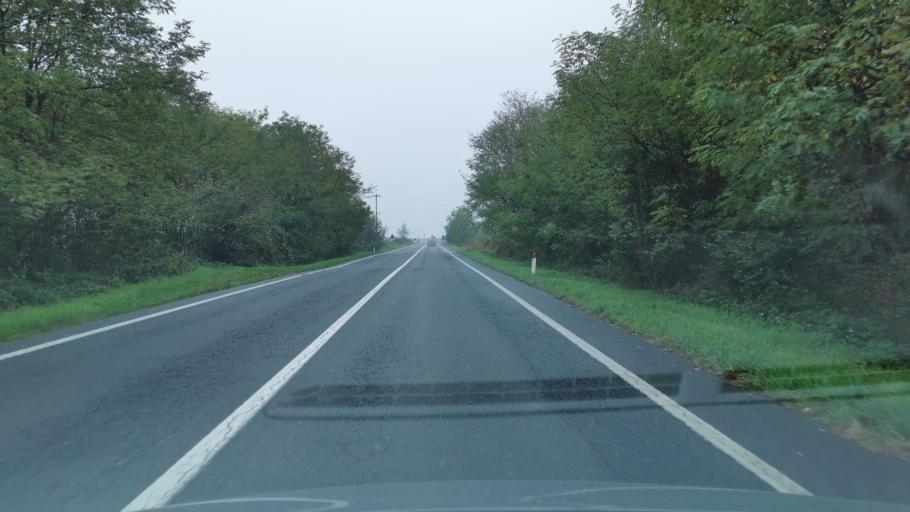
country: IT
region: Piedmont
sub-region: Provincia di Torino
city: Strambino
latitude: 45.3834
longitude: 7.8990
